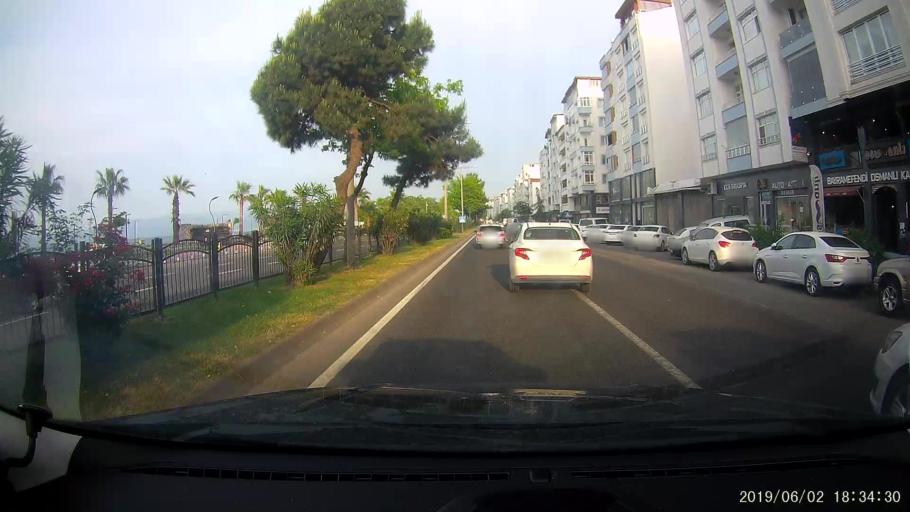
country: TR
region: Ordu
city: Fatsa
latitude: 41.0292
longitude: 37.5049
